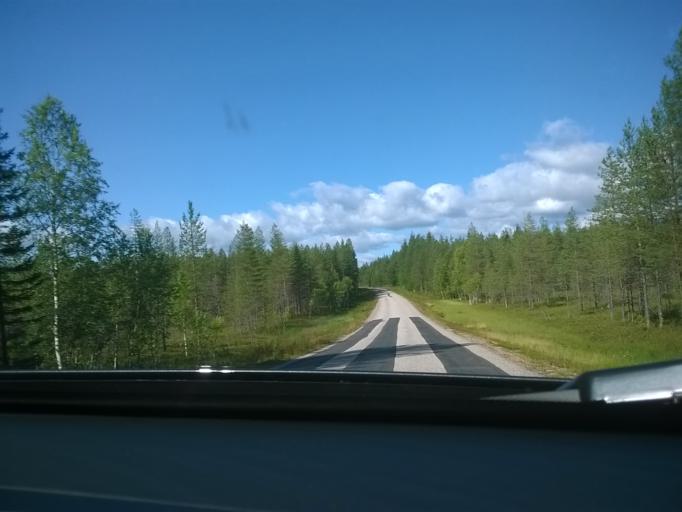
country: FI
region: Kainuu
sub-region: Kehys-Kainuu
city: Kuhmo
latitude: 64.4597
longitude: 29.6358
